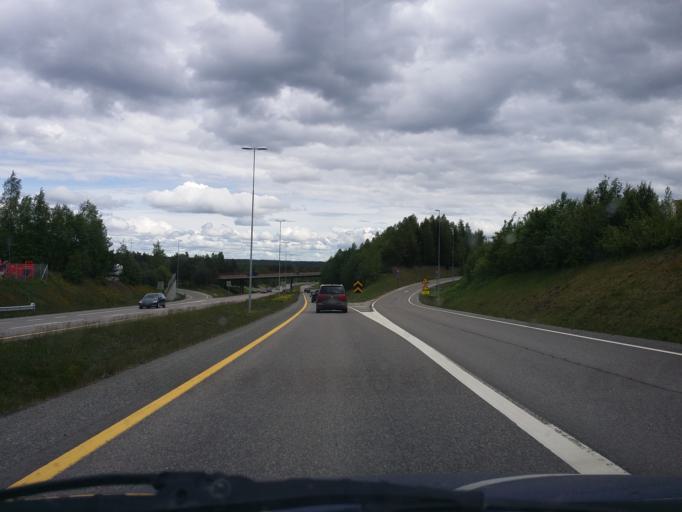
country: NO
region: Hedmark
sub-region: Hamar
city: Hamar
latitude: 60.8421
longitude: 11.0454
